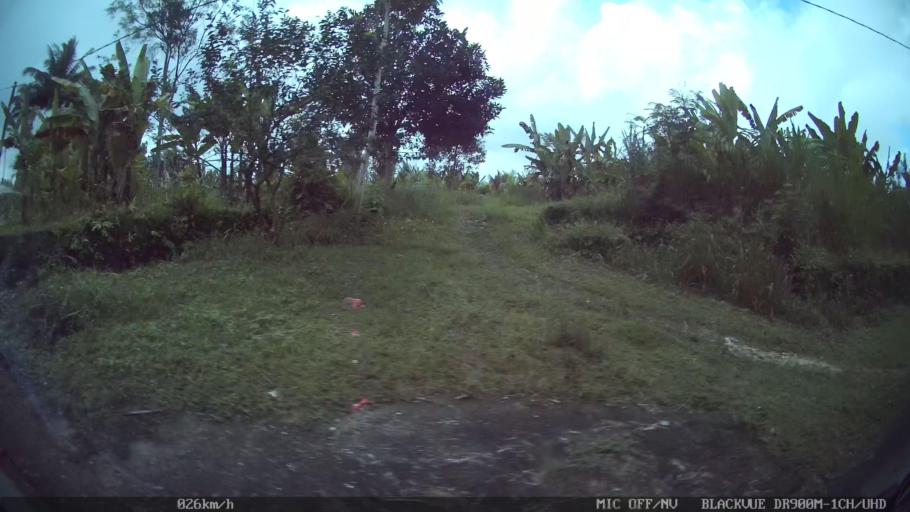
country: ID
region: Bali
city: Badung
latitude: -8.4257
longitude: 115.2265
